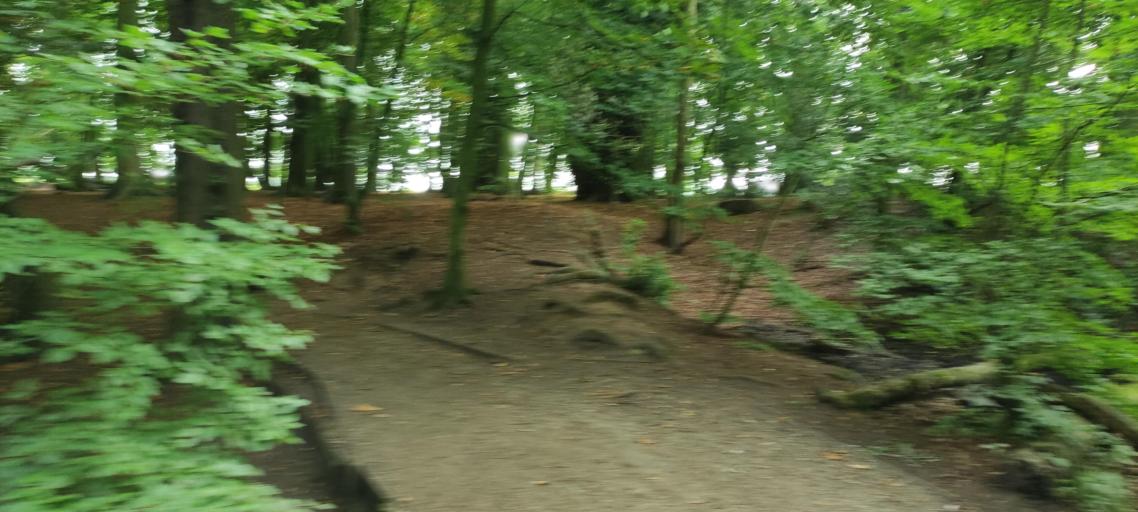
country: GB
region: England
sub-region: Lancashire
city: Leyland
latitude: 53.6813
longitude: -2.7073
